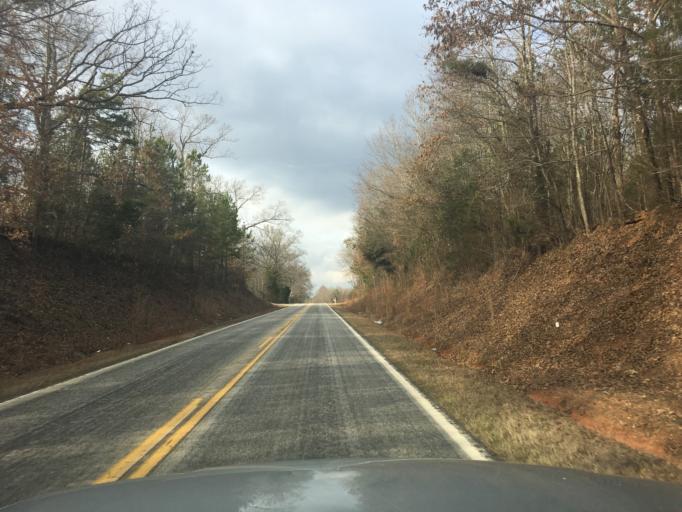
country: US
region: South Carolina
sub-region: Abbeville County
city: Due West
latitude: 34.2649
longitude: -82.4181
